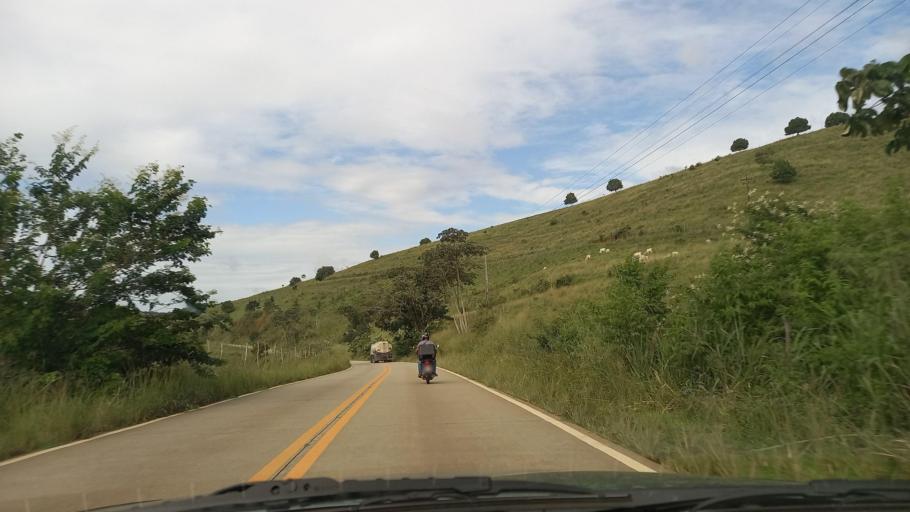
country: BR
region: Pernambuco
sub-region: Maraial
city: Maraial
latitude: -8.7503
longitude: -35.8219
